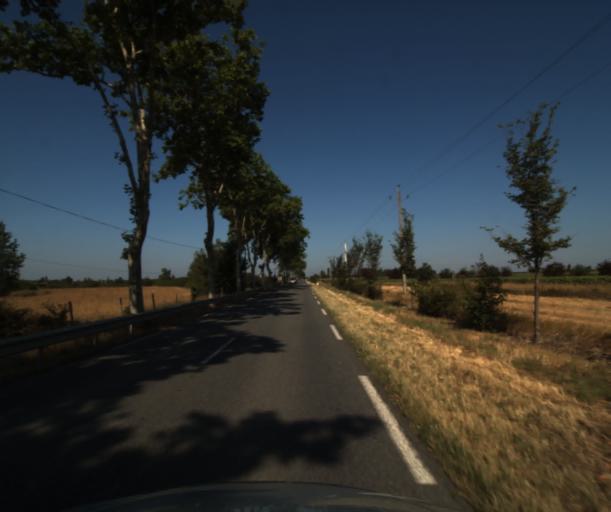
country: FR
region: Midi-Pyrenees
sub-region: Departement de la Haute-Garonne
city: Labastidette
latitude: 43.4663
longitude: 1.2642
